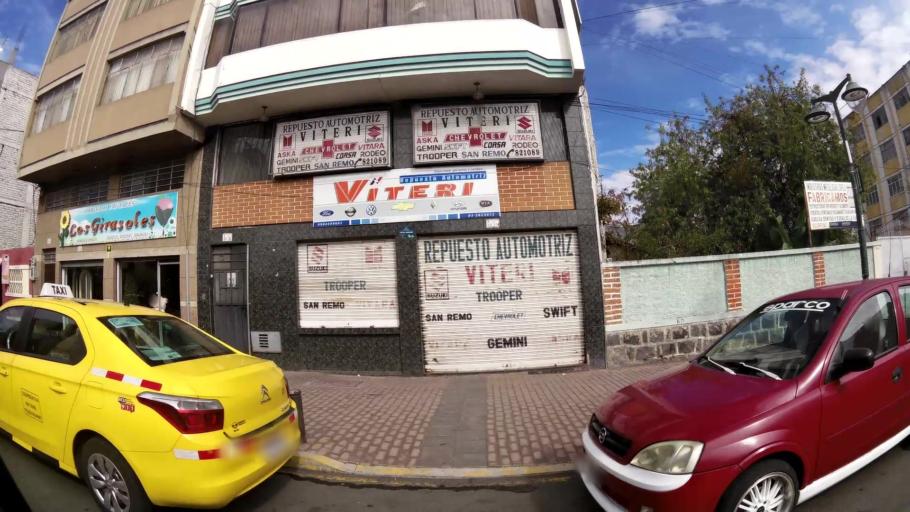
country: EC
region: Tungurahua
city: Ambato
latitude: -1.2335
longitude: -78.6312
